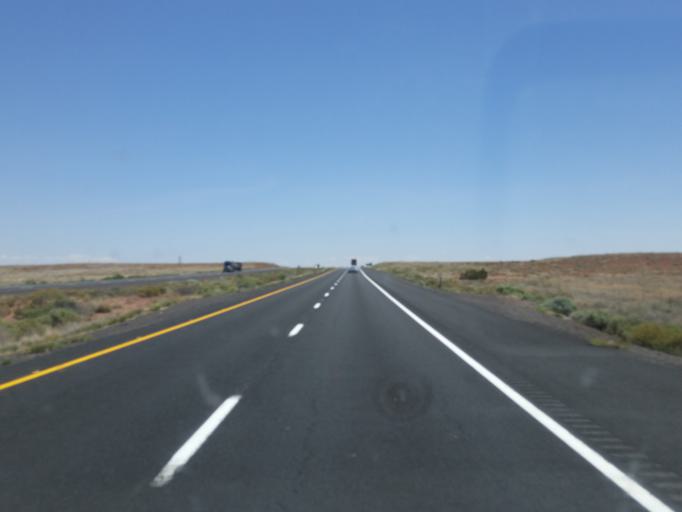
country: US
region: Arizona
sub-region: Coconino County
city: LeChee
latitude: 35.1134
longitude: -111.0621
